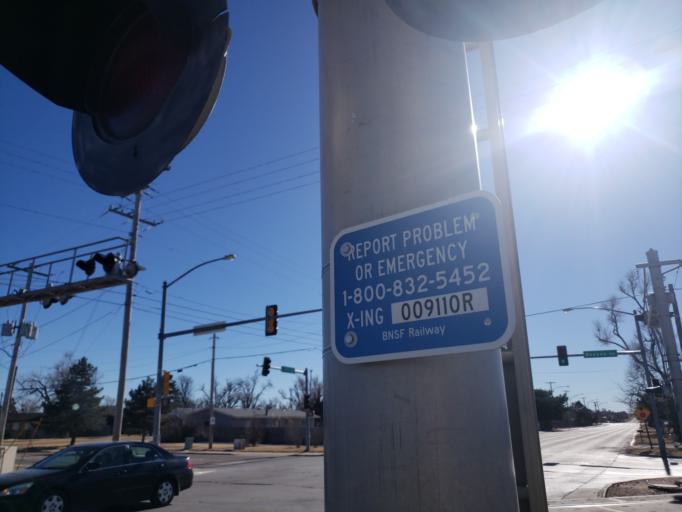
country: US
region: Kansas
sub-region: Ford County
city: Dodge City
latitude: 37.7366
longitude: -100.0333
